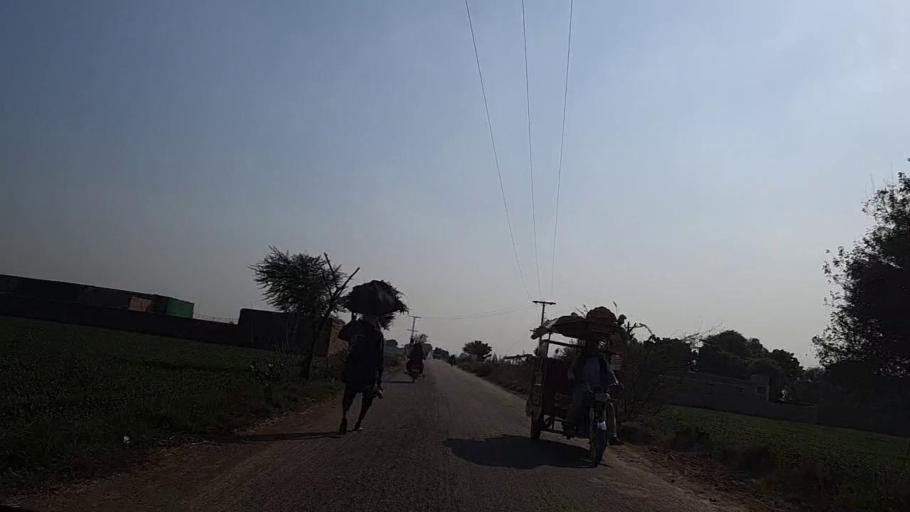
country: PK
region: Sindh
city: Sakrand
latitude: 26.1052
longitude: 68.2907
